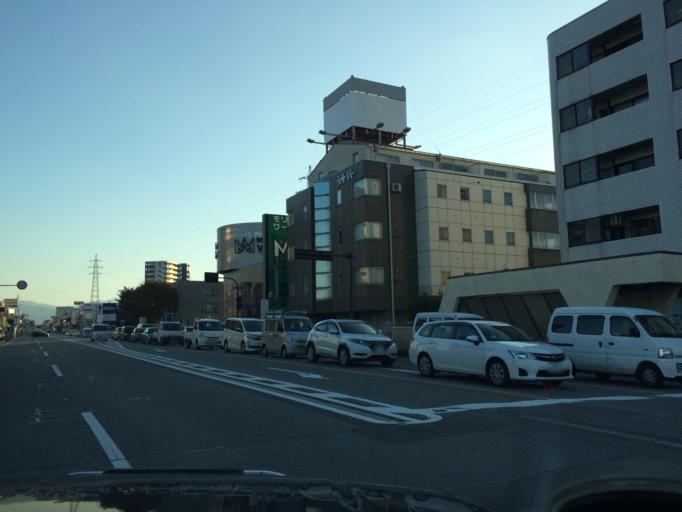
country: JP
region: Toyama
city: Toyama-shi
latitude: 36.6741
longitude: 137.2108
